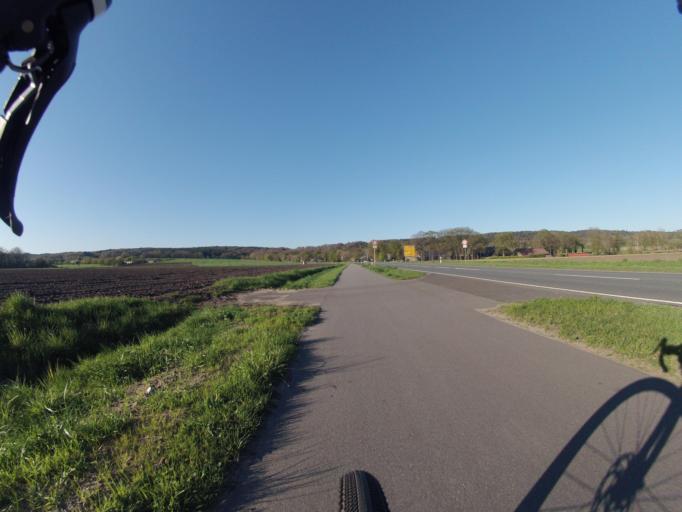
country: DE
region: North Rhine-Westphalia
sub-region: Regierungsbezirk Munster
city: Birgte
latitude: 52.2364
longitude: 7.6922
